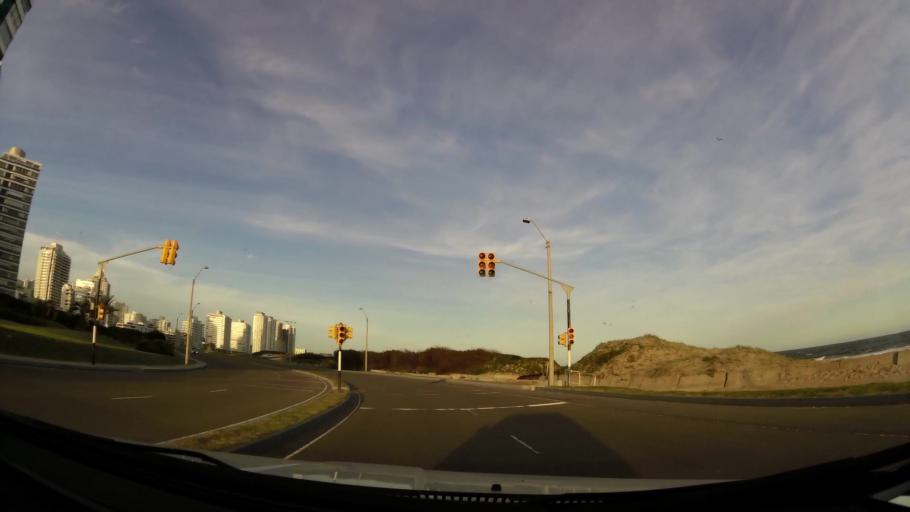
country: UY
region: Maldonado
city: Punta del Este
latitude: -34.9537
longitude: -54.9299
